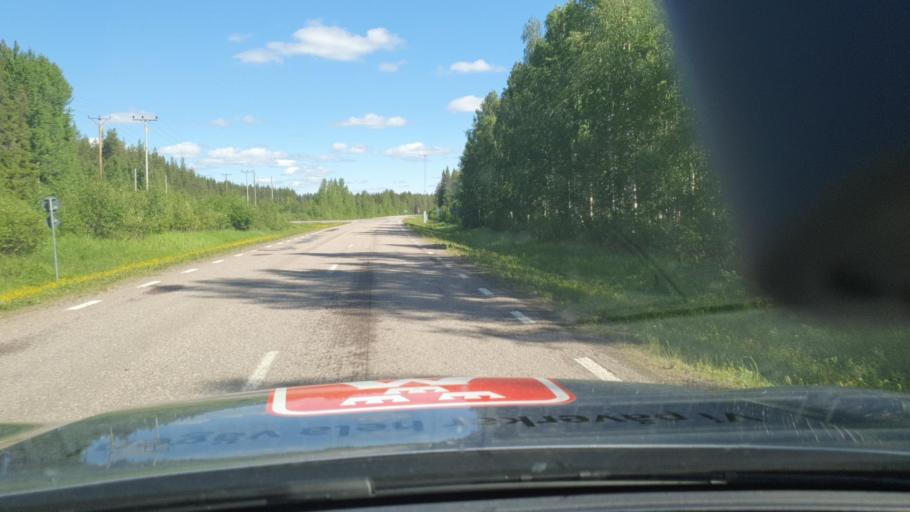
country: SE
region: Norrbotten
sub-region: Overkalix Kommun
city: OEverkalix
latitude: 67.0697
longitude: 22.5208
